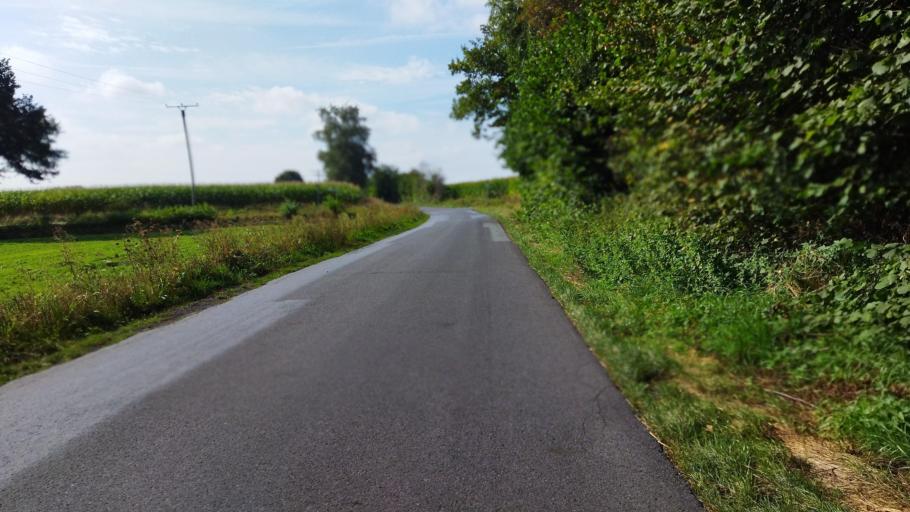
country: DE
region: North Rhine-Westphalia
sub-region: Regierungsbezirk Munster
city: Sassenberg
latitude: 51.9886
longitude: 8.0087
